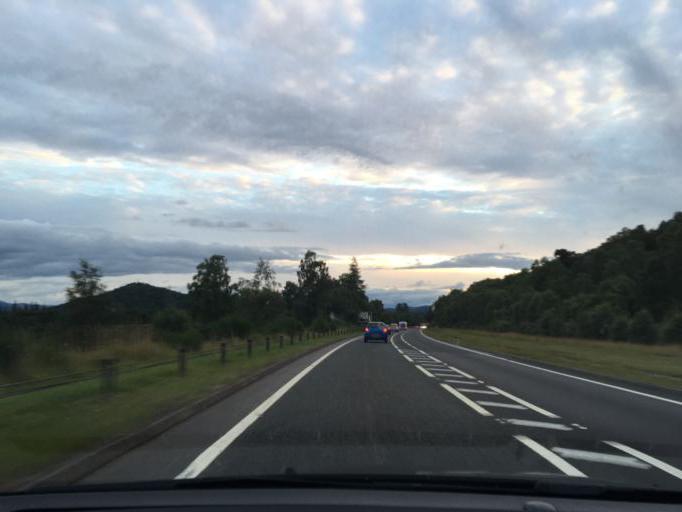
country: GB
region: Scotland
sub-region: Highland
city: Aviemore
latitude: 57.1759
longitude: -3.8394
